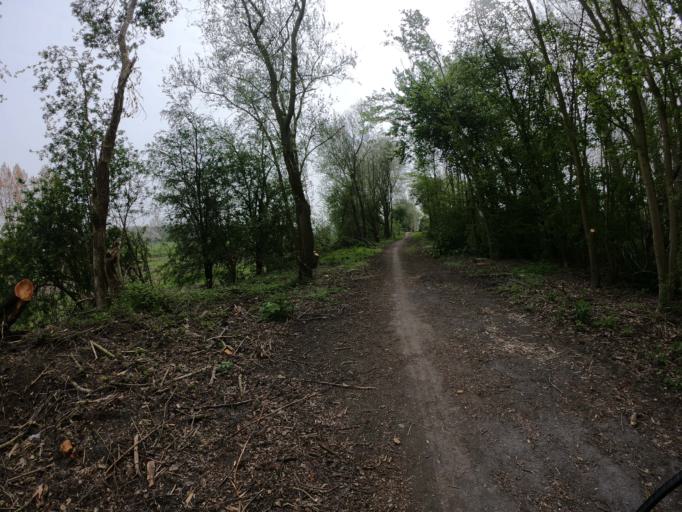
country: BE
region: Flanders
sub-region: Provincie West-Vlaanderen
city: Avelgem
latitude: 50.7677
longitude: 3.4481
